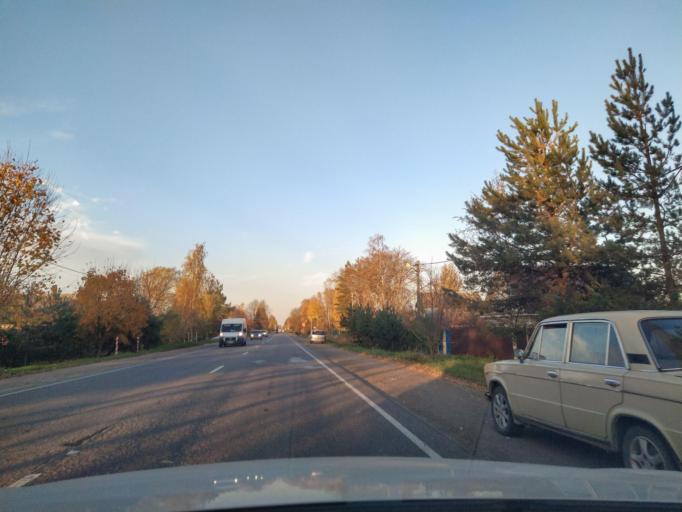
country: RU
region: Leningrad
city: Maloye Verevo
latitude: 59.6138
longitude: 30.2029
